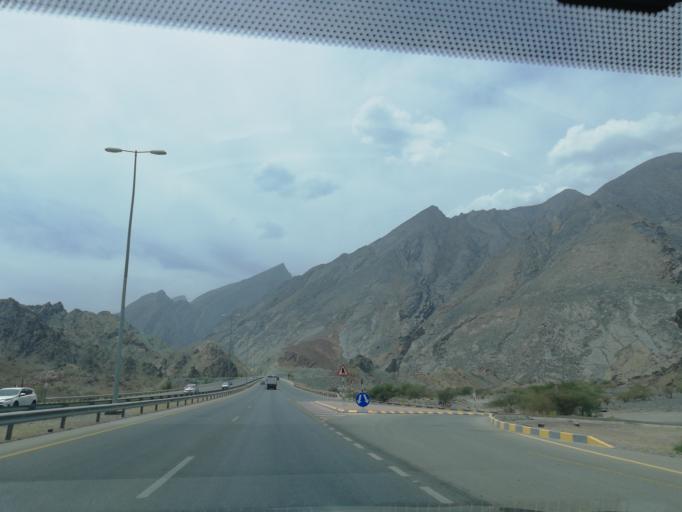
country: OM
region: Muhafazat ad Dakhiliyah
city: Sufalat Sama'il
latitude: 23.1861
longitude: 57.8614
